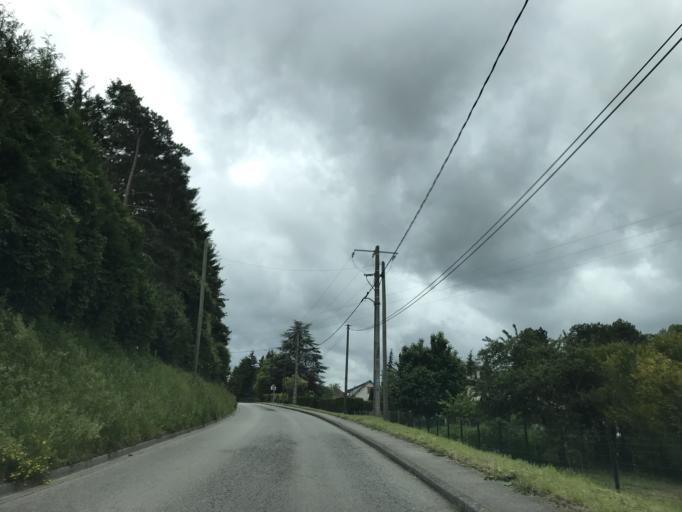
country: FR
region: Haute-Normandie
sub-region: Departement de l'Eure
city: Garennes-sur-Eure
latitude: 48.9076
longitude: 1.4349
